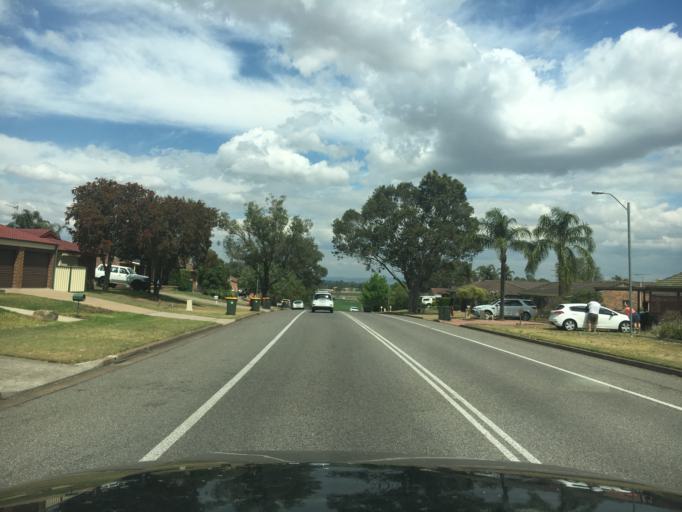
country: AU
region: New South Wales
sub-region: Singleton
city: Singleton
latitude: -32.5457
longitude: 151.1718
